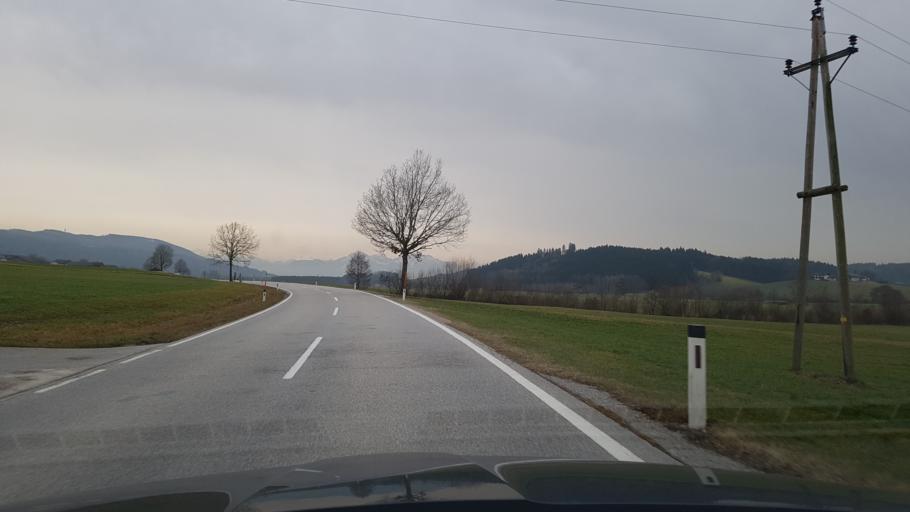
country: AT
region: Salzburg
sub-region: Politischer Bezirk Salzburg-Umgebung
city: Nussdorf am Haunsberg
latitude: 47.9848
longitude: 13.0129
